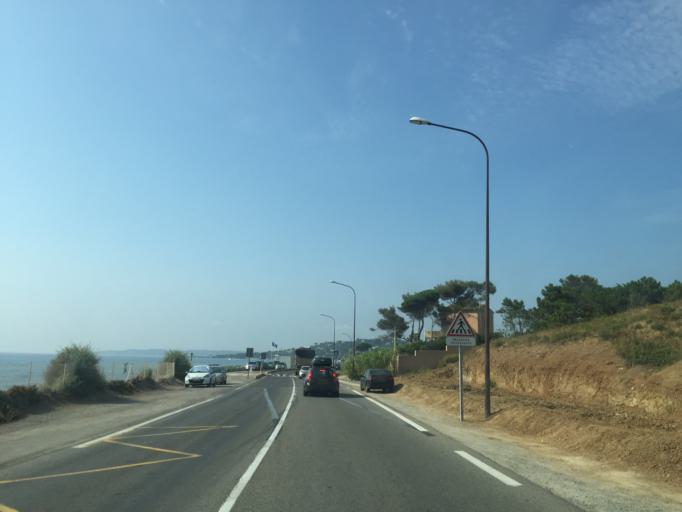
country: FR
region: Provence-Alpes-Cote d'Azur
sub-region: Departement du Var
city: Sainte-Maxime
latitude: 43.3325
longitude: 6.6687
